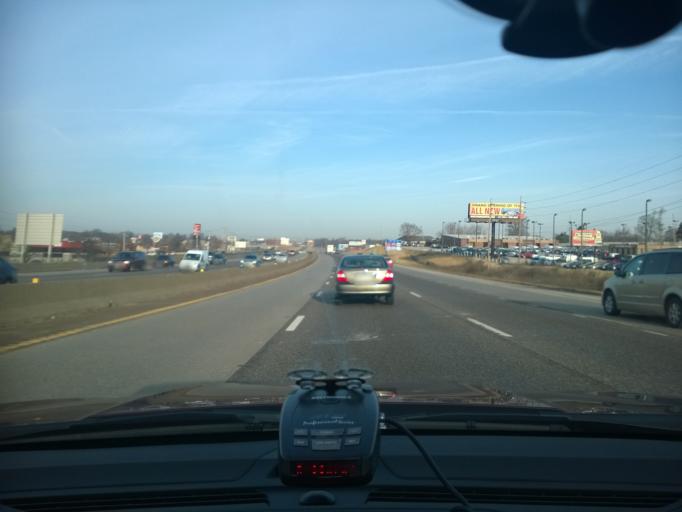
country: US
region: Missouri
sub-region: Saint Charles County
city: Saint Charles
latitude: 38.7833
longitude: -90.5223
